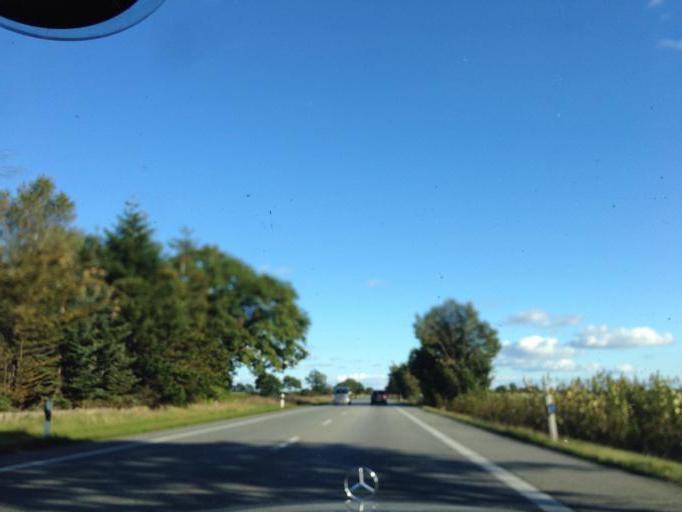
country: DE
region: Schleswig-Holstein
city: Wahlstedt
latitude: 53.9818
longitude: 10.2015
